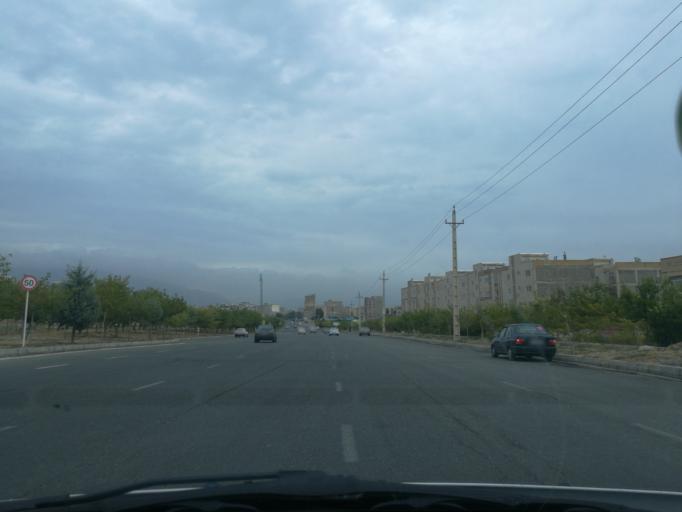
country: IR
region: Alborz
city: Karaj
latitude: 35.8635
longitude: 50.9309
